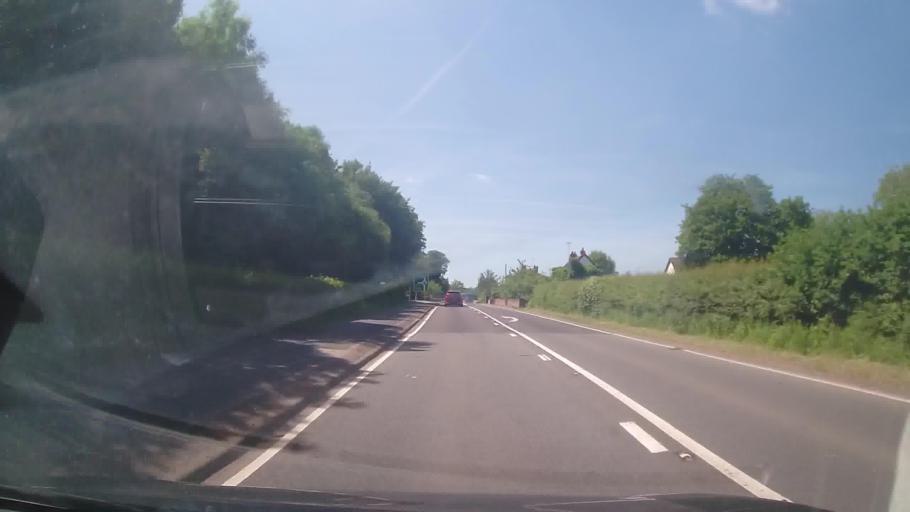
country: GB
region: England
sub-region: Herefordshire
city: Leominster
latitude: 52.2359
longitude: -2.7257
